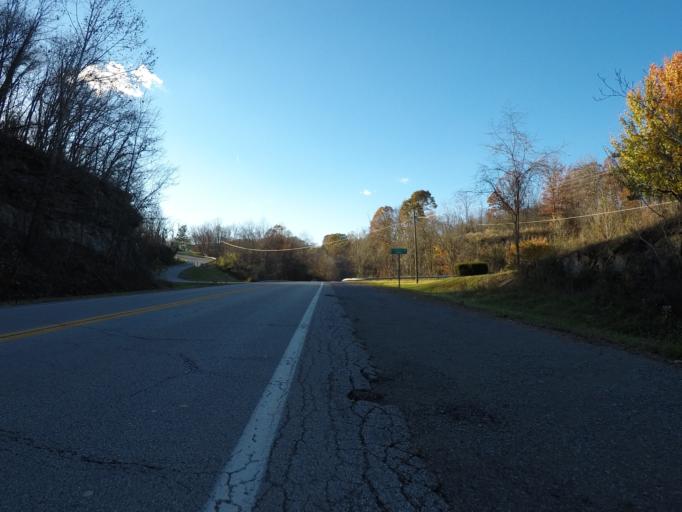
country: US
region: West Virginia
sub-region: Wayne County
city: Ceredo
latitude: 38.3827
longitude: -82.5665
